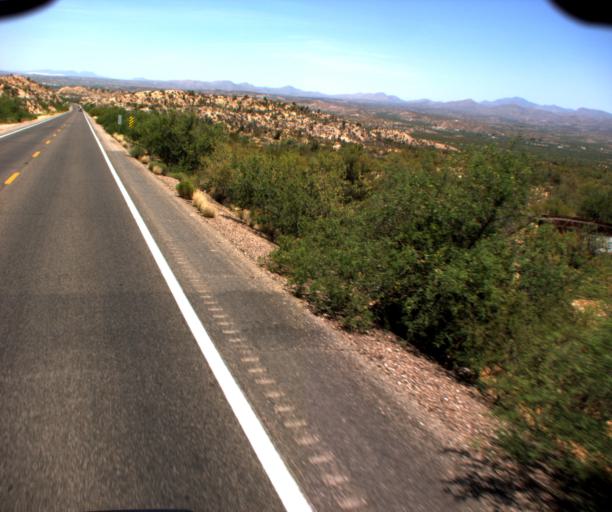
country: US
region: Arizona
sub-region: Gila County
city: San Carlos
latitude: 33.3409
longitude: -110.6018
